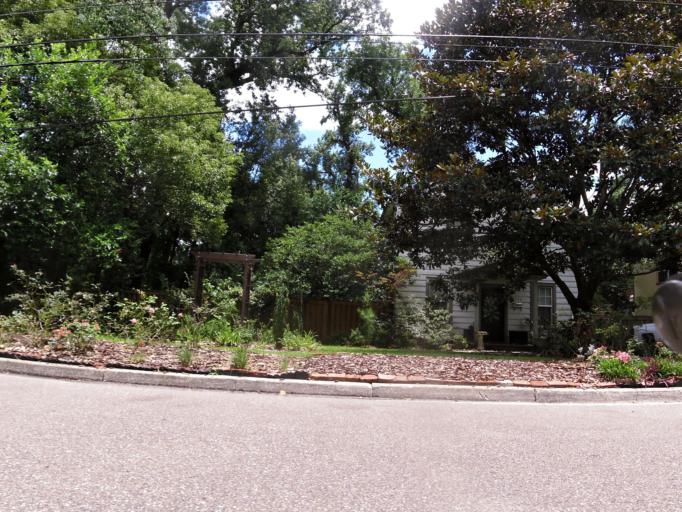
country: US
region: Florida
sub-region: Duval County
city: Jacksonville
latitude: 30.3087
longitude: -81.7032
